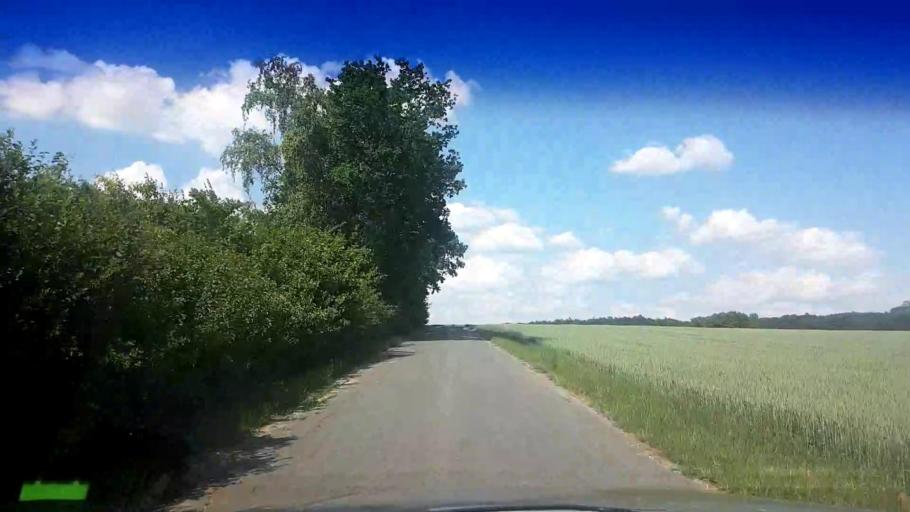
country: DE
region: Bavaria
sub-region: Upper Franconia
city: Litzendorf
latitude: 49.9410
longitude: 11.0110
